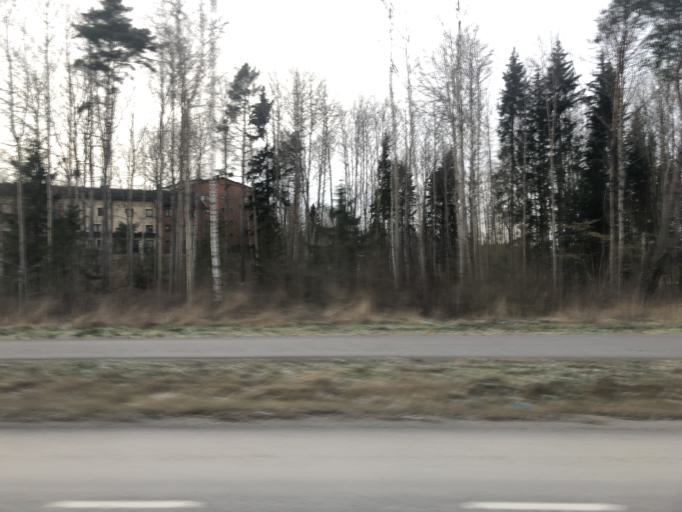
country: SE
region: Stockholm
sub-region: Jarfalla Kommun
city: Jakobsberg
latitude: 59.4156
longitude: 17.7995
